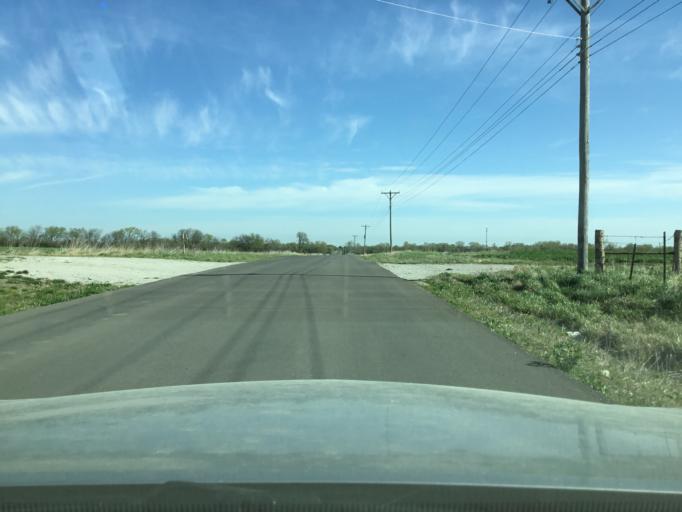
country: US
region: Kansas
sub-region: Neosho County
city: Chanute
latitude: 37.6492
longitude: -95.4435
